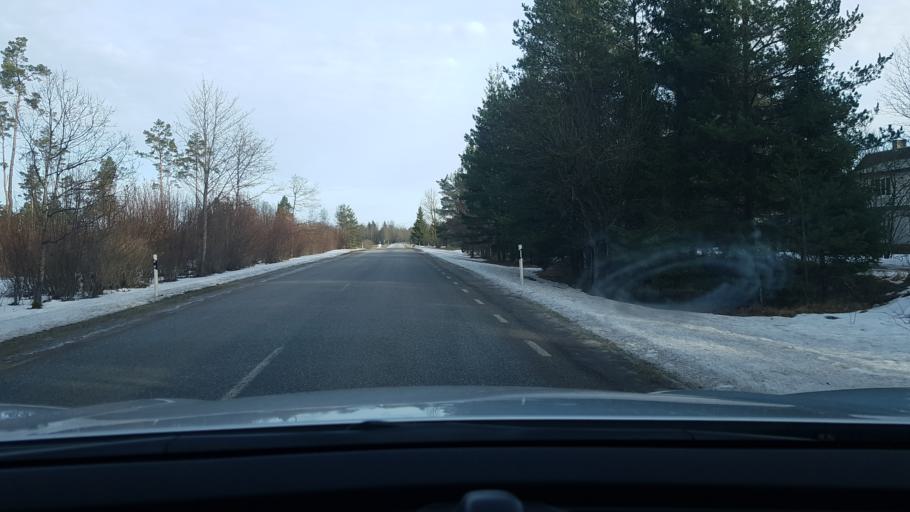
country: EE
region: Saare
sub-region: Kuressaare linn
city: Kuressaare
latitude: 58.4148
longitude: 22.6597
